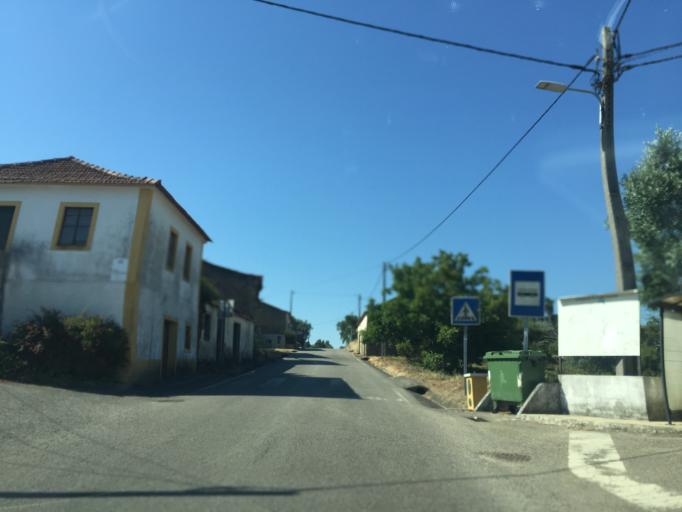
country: PT
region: Santarem
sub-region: Tomar
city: Tomar
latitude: 39.5829
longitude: -8.3275
